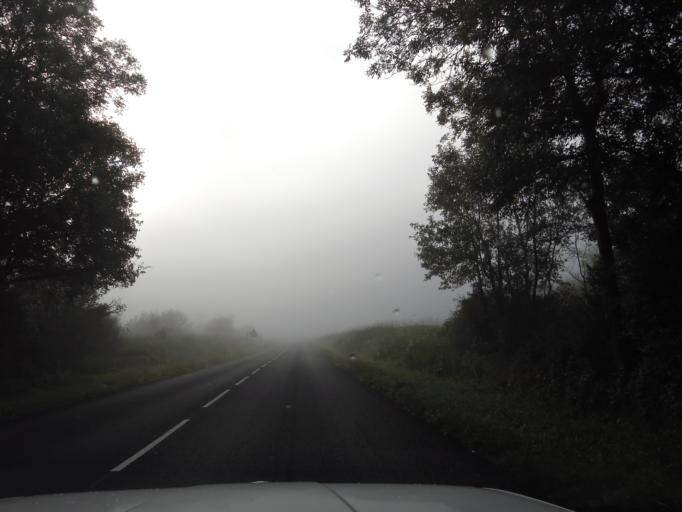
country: FR
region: Rhone-Alpes
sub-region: Departement de l'Isere
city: Creys-Mepieu
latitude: 45.7523
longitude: 5.5009
